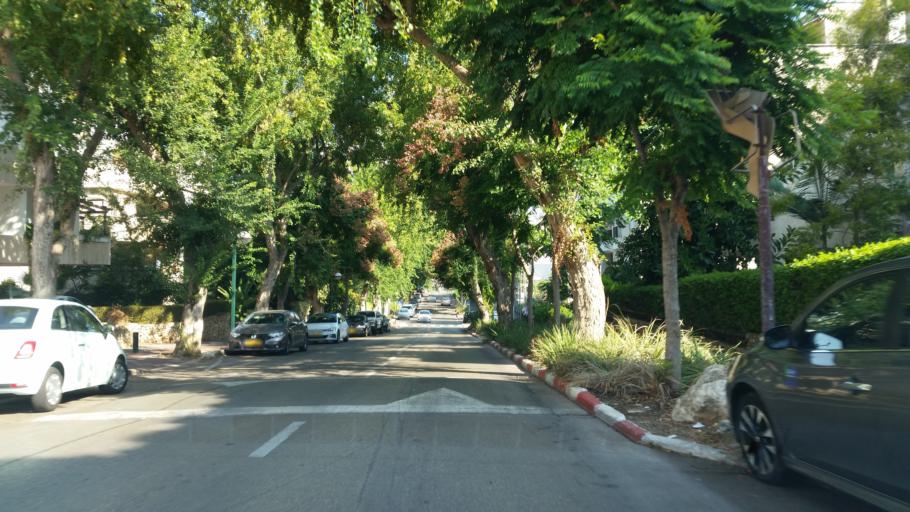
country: IL
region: Tel Aviv
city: Ramat HaSharon
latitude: 32.1477
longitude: 34.8458
